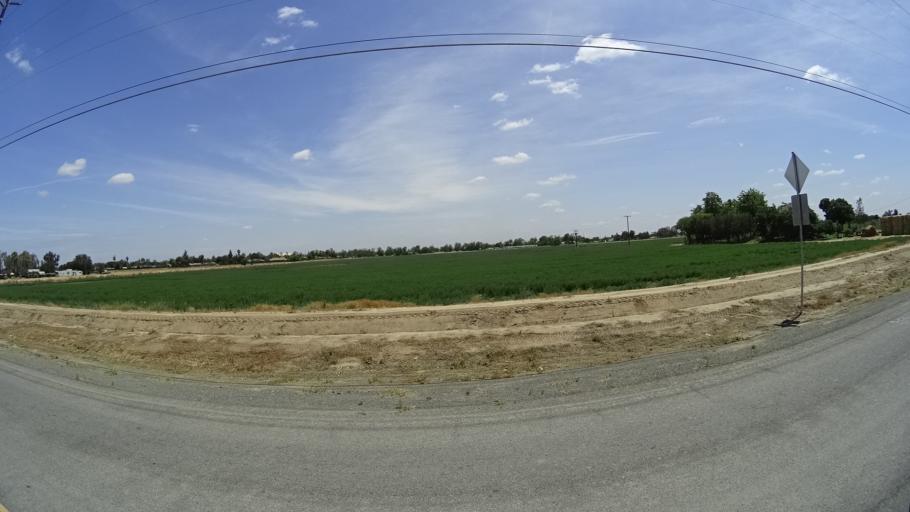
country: US
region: California
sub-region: Kings County
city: Home Garden
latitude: 36.3084
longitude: -119.6460
